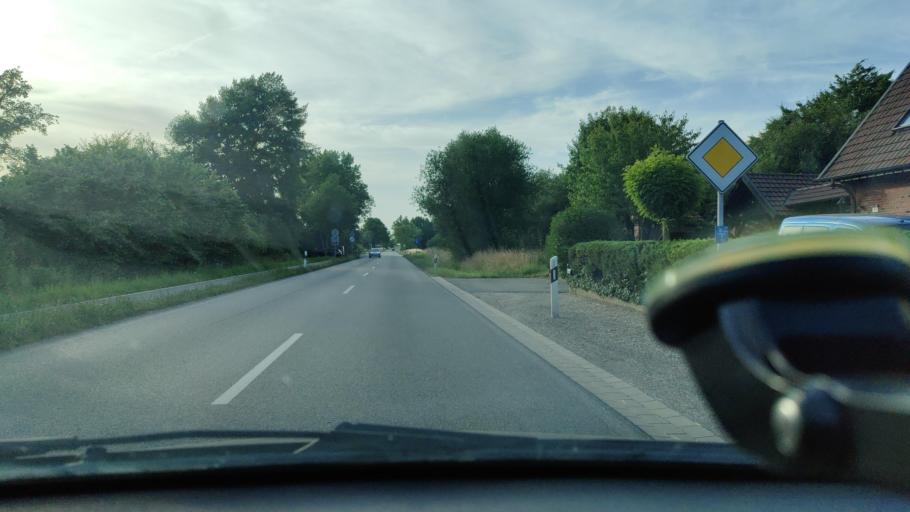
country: DE
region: North Rhine-Westphalia
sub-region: Regierungsbezirk Munster
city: Coesfeld
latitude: 52.0114
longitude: 7.1898
